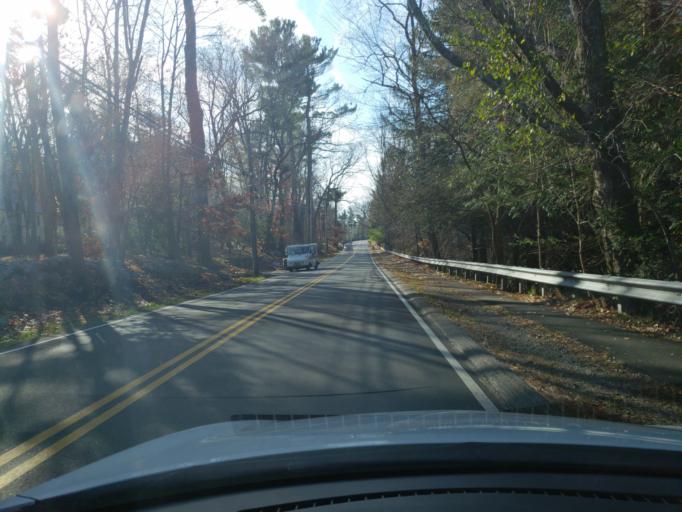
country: US
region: Massachusetts
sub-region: Essex County
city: Andover
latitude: 42.6465
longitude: -71.1436
